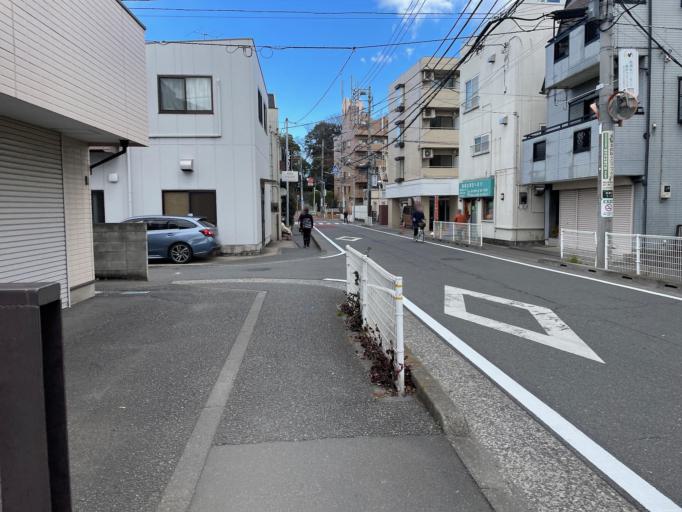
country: JP
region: Tokyo
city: Chofugaoka
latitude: 35.6520
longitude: 139.5273
